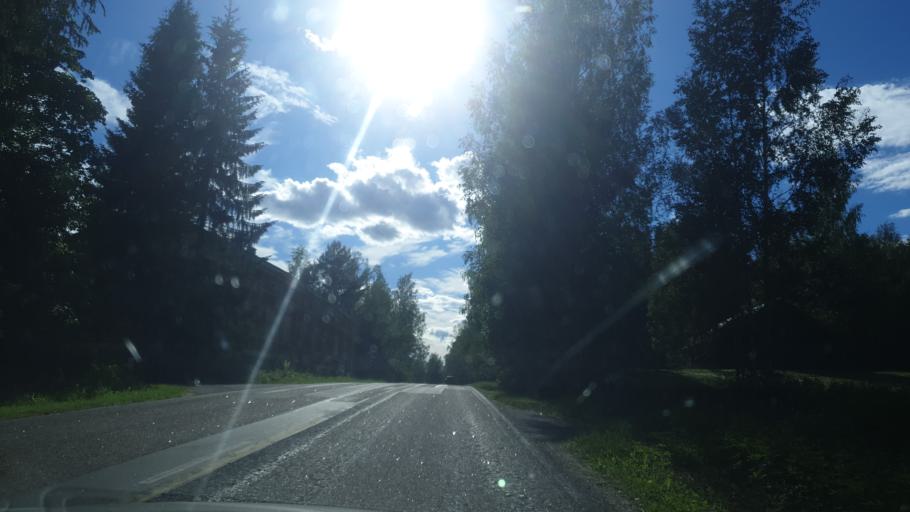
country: FI
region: Southern Savonia
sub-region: Mikkeli
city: Pertunmaa
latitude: 61.5233
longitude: 26.5148
